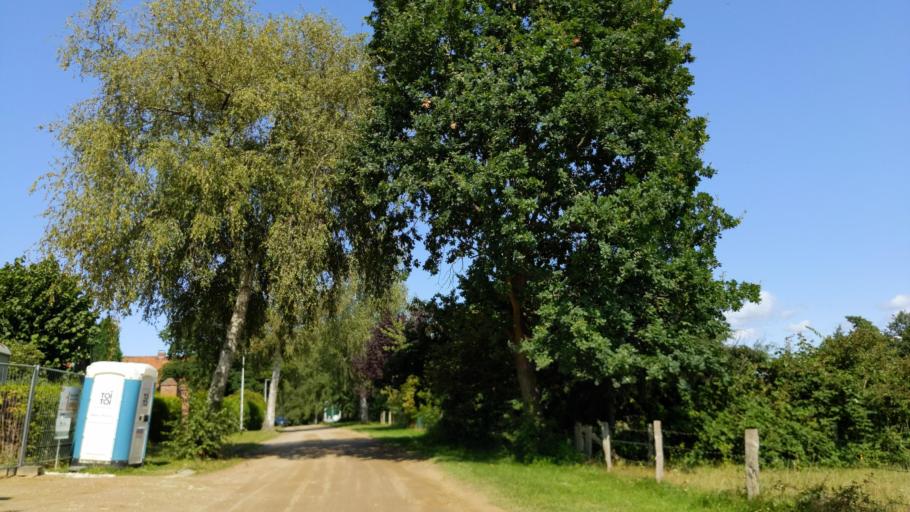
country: DE
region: Schleswig-Holstein
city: Bosdorf
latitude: 54.1685
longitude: 10.4891
